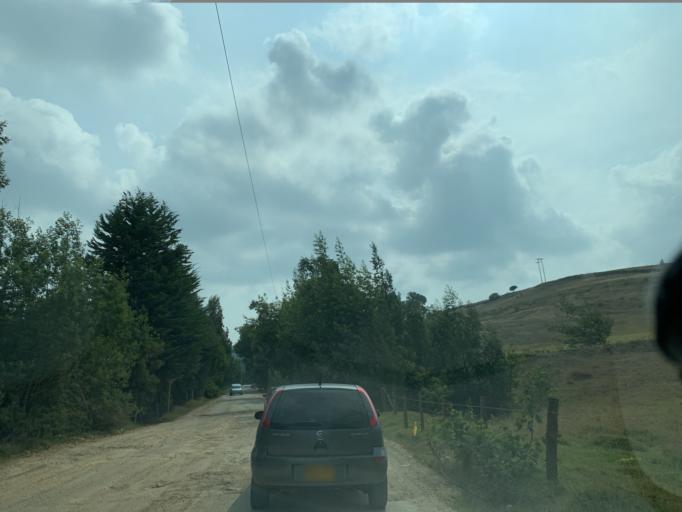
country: CO
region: Boyaca
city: Siachoque
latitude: 5.5512
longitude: -73.2933
